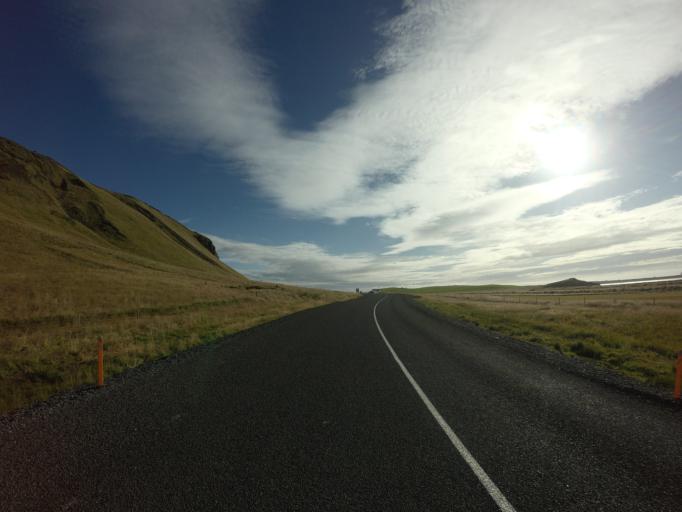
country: IS
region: South
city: Vestmannaeyjar
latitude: 63.4114
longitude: -19.0479
